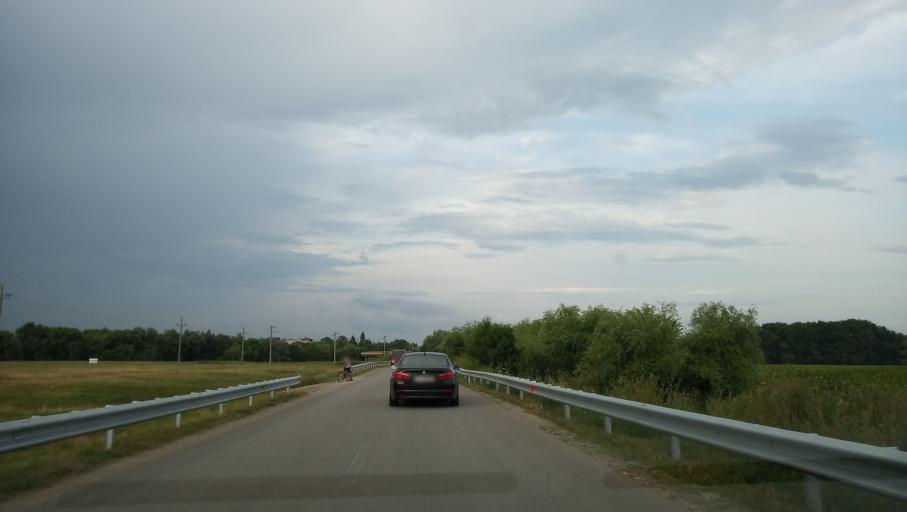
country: RO
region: Giurgiu
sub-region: Comuna Singureni
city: Singureni
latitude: 44.2295
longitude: 25.9338
